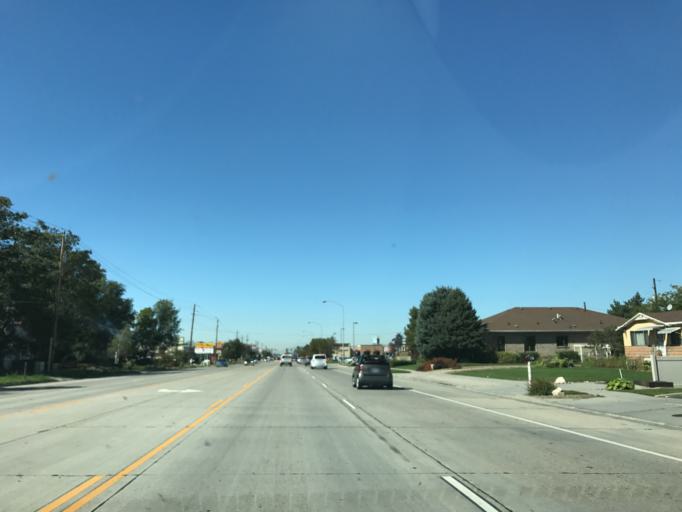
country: US
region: Utah
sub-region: Weber County
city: Ogden
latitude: 41.2443
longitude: -111.9657
